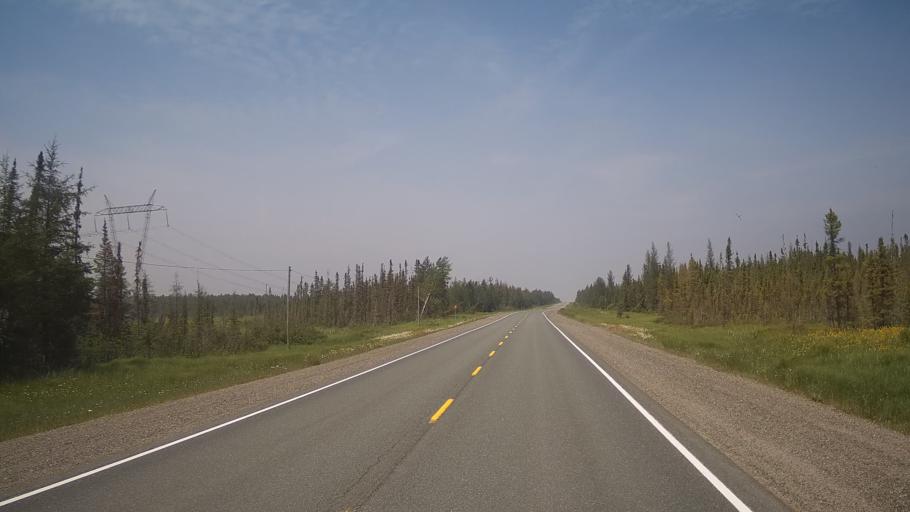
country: CA
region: Ontario
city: Timmins
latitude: 48.7643
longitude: -81.3616
